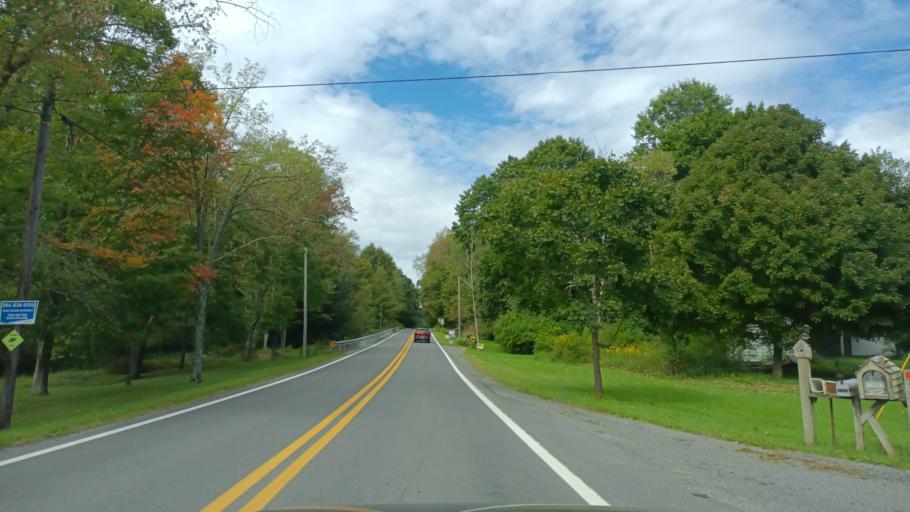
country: US
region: Maryland
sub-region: Garrett County
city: Oakland
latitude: 39.3189
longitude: -79.4890
